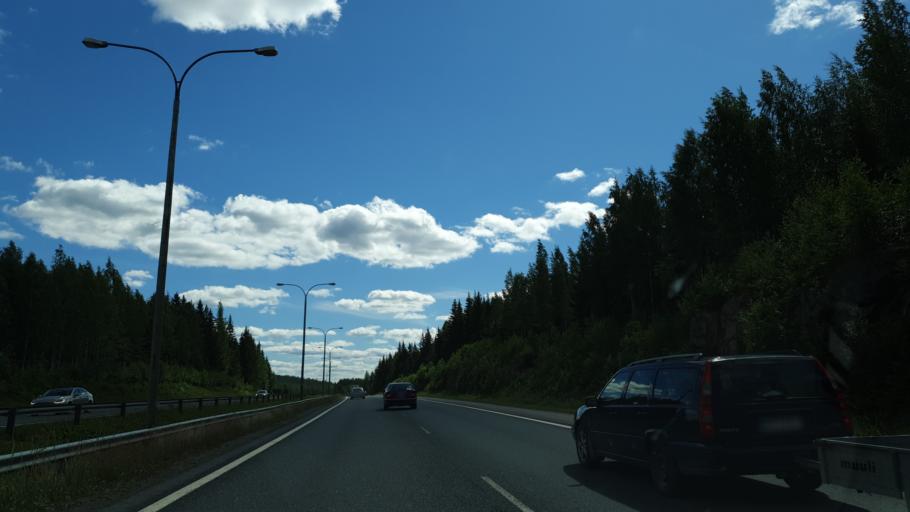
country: FI
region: Northern Savo
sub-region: Kuopio
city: Siilinjaervi
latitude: 63.0278
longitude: 27.6571
